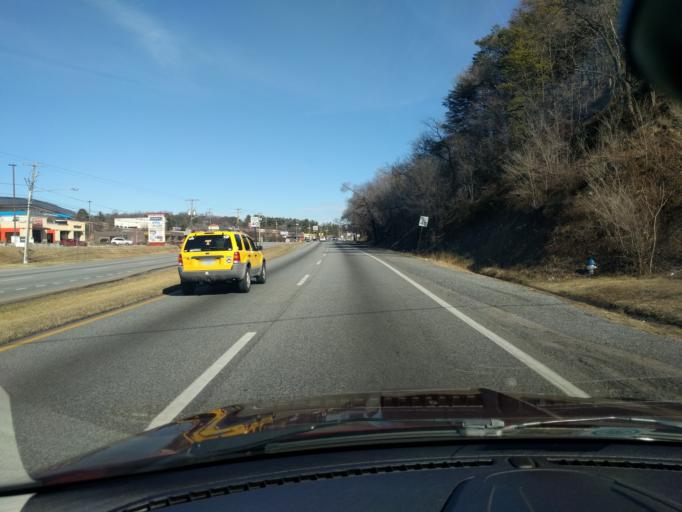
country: US
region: Virginia
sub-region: Roanoke County
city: Vinton
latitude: 37.3023
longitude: -79.8927
